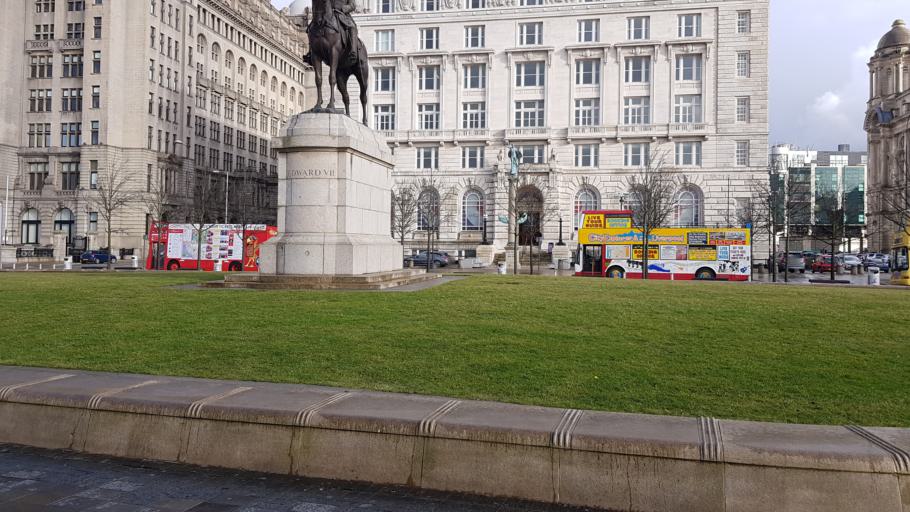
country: GB
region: England
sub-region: Liverpool
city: Liverpool
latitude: 53.4045
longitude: -2.9967
